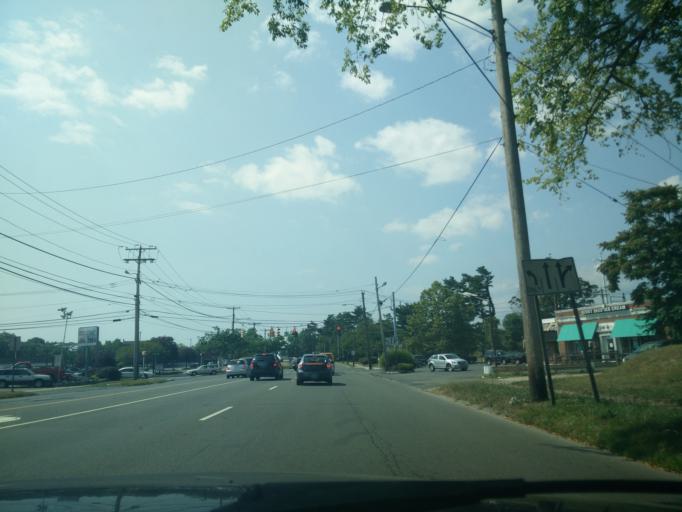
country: US
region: Connecticut
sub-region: Fairfield County
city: Fairfield
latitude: 41.1476
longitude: -73.2486
